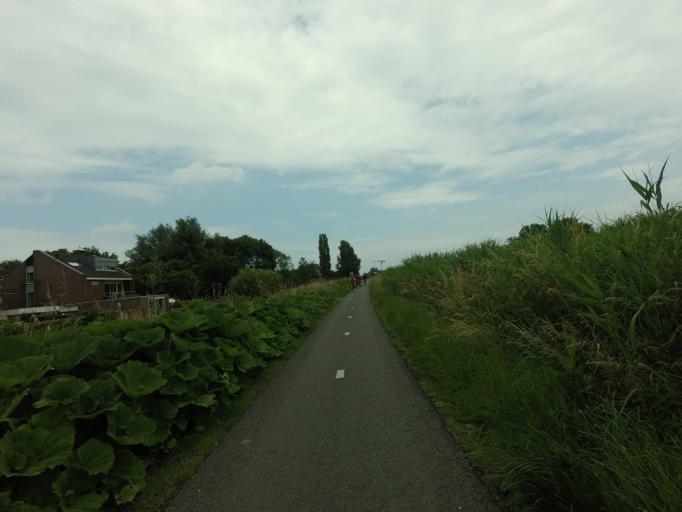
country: NL
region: North Holland
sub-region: Gemeente Purmerend
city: Purmerend
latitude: 52.4903
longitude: 4.9571
